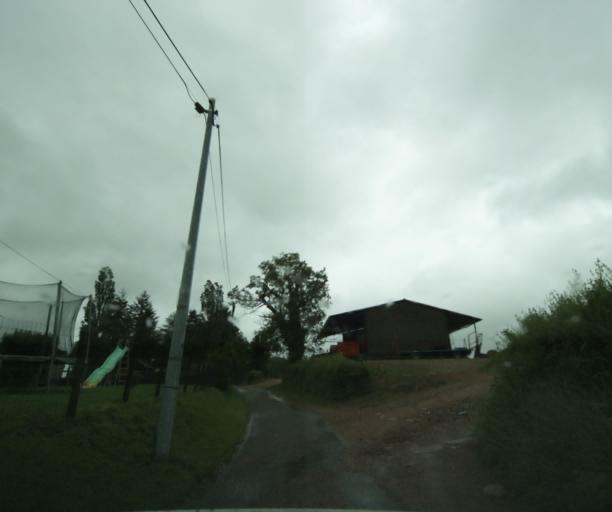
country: FR
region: Bourgogne
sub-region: Departement de Saone-et-Loire
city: Charolles
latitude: 46.5055
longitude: 4.3820
